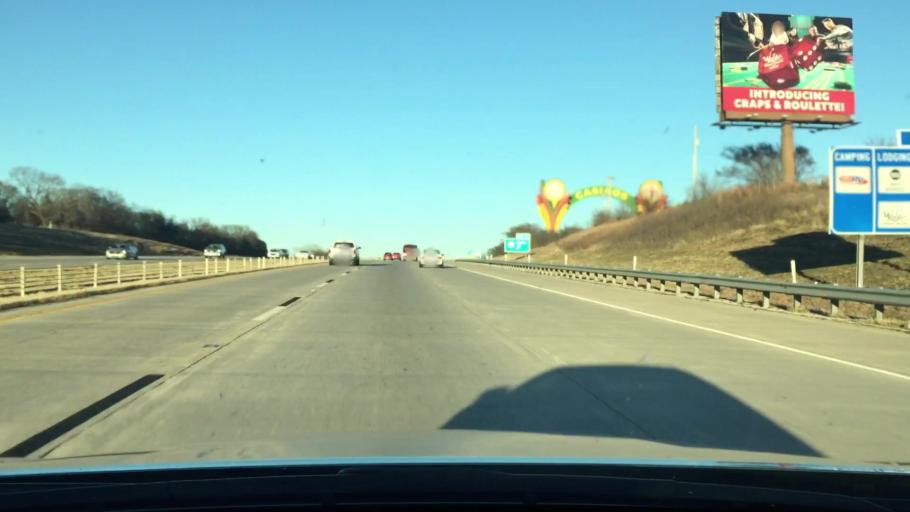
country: US
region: Texas
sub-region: Cooke County
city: Gainesville
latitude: 33.7345
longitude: -97.1508
